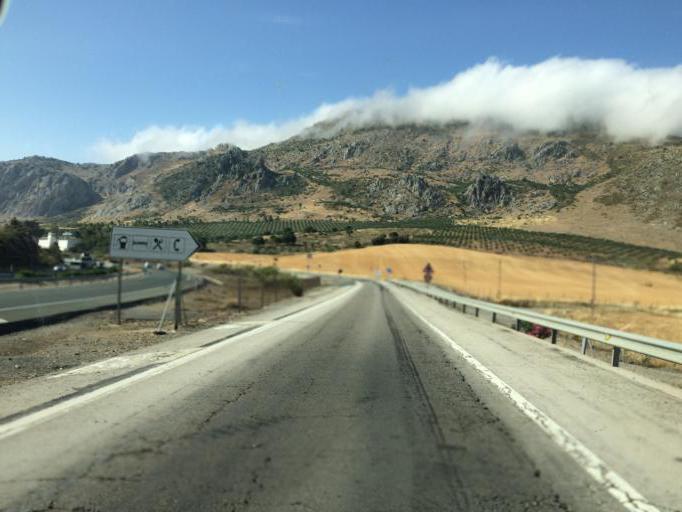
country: ES
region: Andalusia
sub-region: Provincia de Malaga
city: Antequera
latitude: 36.9925
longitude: -4.4728
